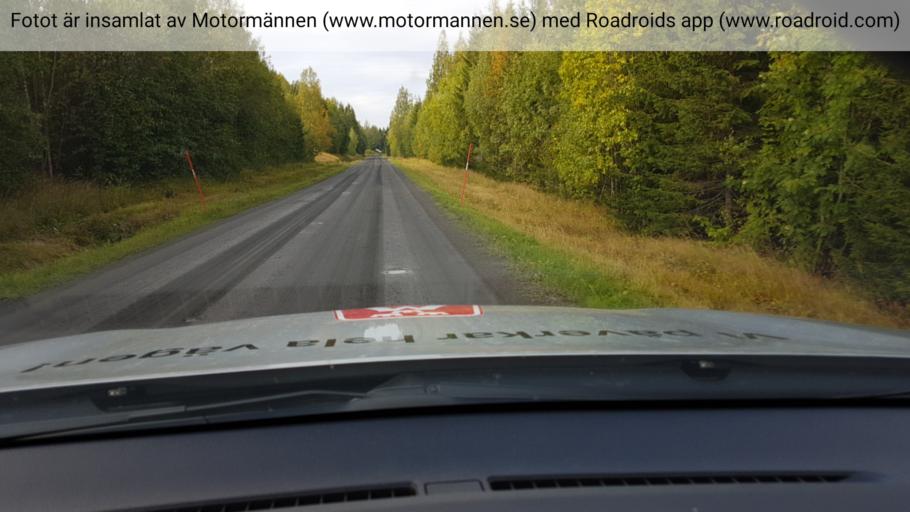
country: SE
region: Jaemtland
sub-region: Stroemsunds Kommun
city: Stroemsund
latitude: 64.1053
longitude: 15.8201
